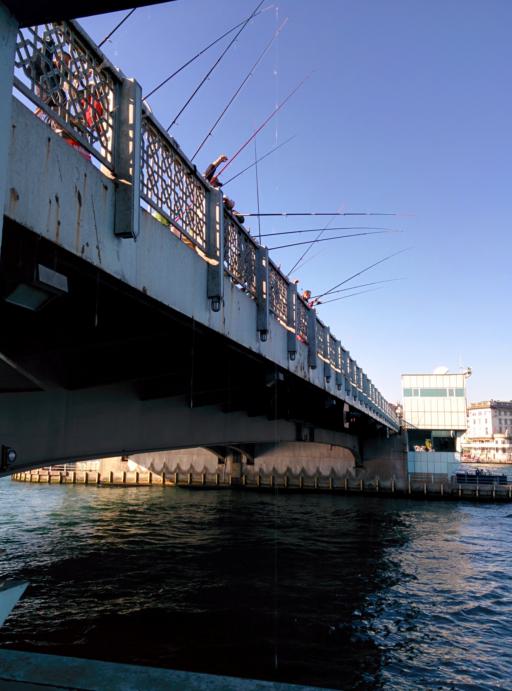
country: TR
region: Istanbul
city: Eminoenue
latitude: 41.0147
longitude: 28.9726
